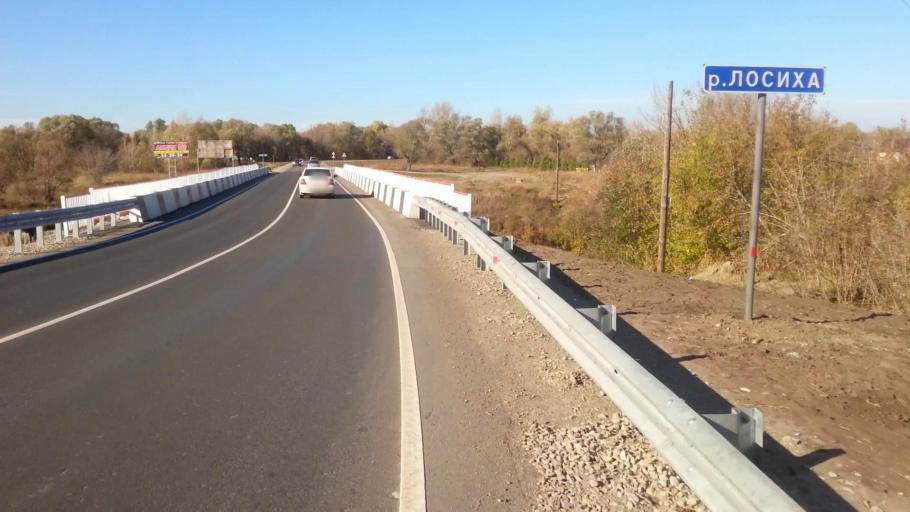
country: RU
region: Altai Krai
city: Sannikovo
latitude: 53.3195
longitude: 83.9444
